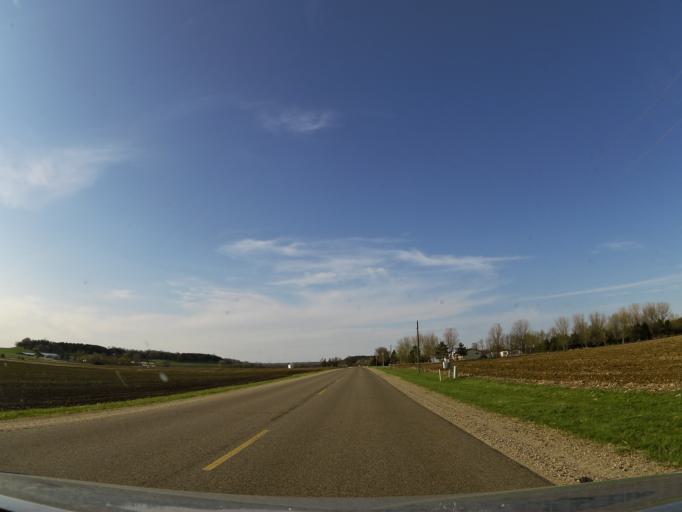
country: US
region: Wisconsin
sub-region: Pierce County
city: River Falls
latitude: 44.8123
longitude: -92.6448
